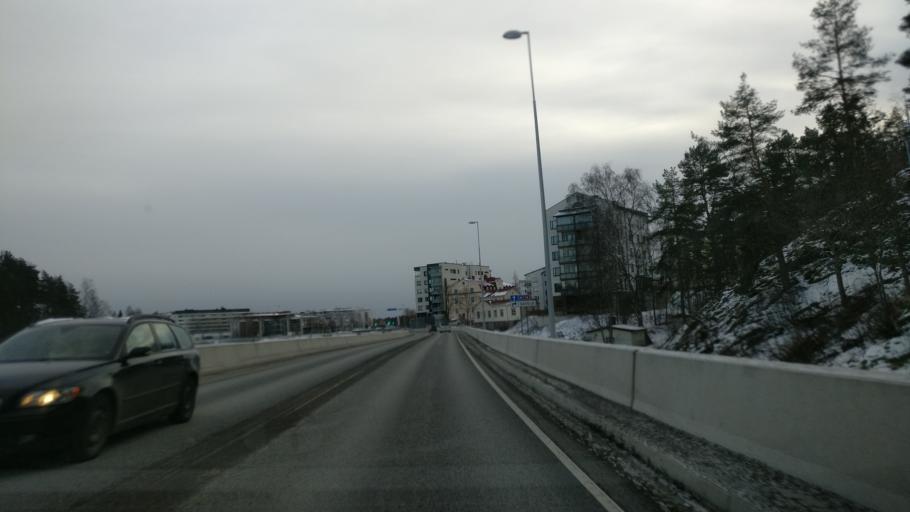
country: FI
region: Southern Savonia
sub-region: Savonlinna
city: Savonlinna
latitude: 61.8727
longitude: 28.8813
